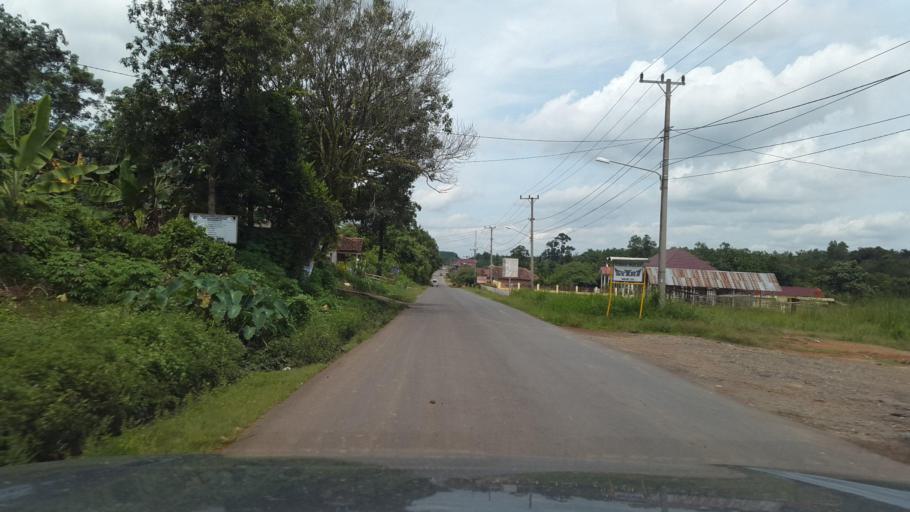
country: ID
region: South Sumatra
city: Gunungmegang Dalam
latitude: -3.3424
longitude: 103.9138
